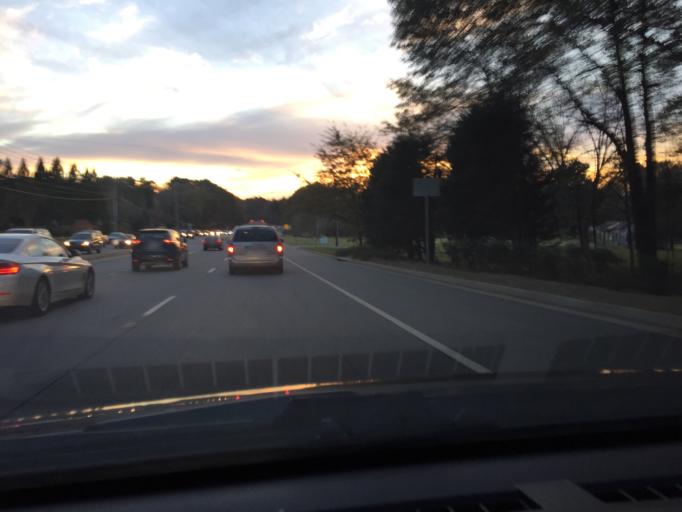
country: US
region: Georgia
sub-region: Gwinnett County
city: Berkeley Lake
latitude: 33.9987
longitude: -84.2001
